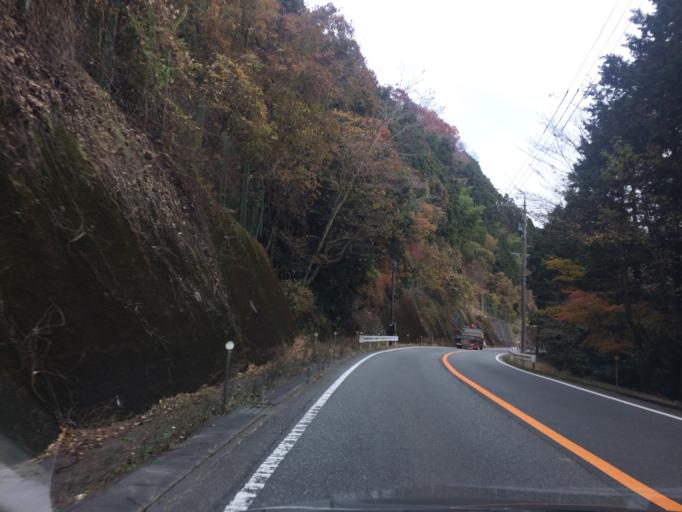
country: JP
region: Shizuoka
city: Fujinomiya
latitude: 35.1920
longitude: 138.5297
